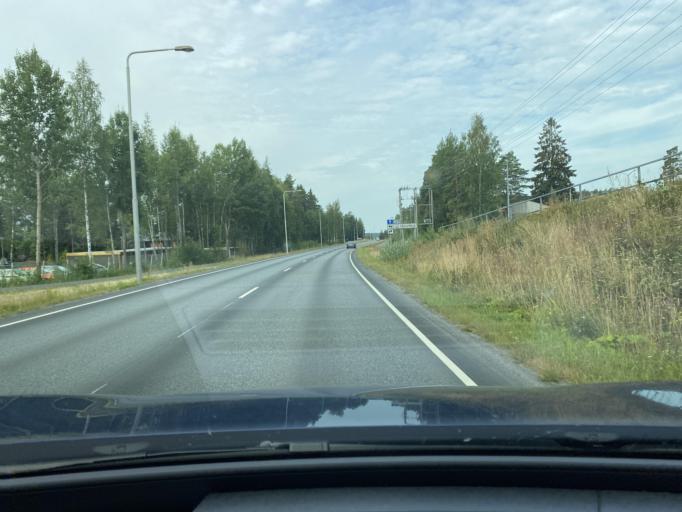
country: FI
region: Pirkanmaa
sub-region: Lounais-Pirkanmaa
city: Vammala
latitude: 61.3546
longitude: 22.8871
